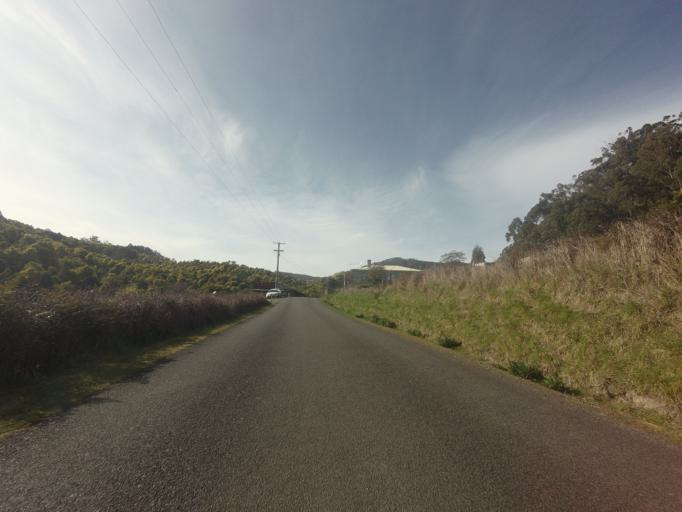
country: AU
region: Tasmania
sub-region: Huon Valley
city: Cygnet
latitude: -43.1753
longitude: 147.1534
